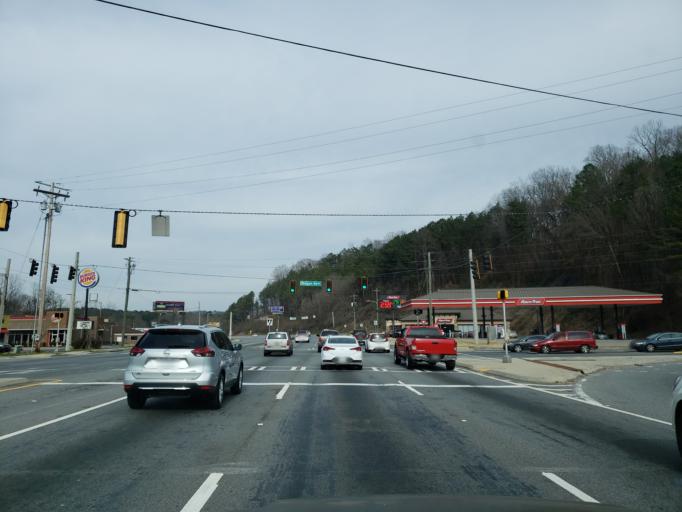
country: US
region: Georgia
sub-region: Whitfield County
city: Dalton
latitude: 34.7948
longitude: -84.9970
